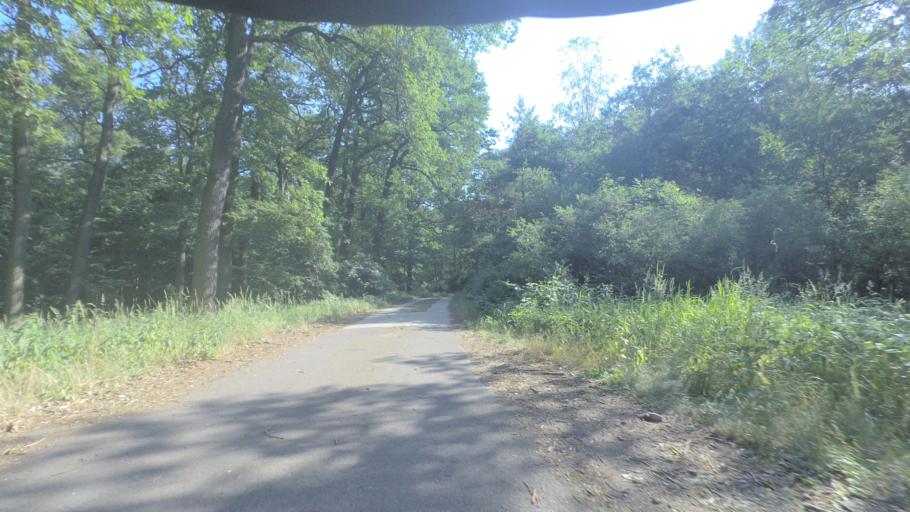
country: DE
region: Saxony-Anhalt
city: Rodleben
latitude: 51.8269
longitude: 12.1624
